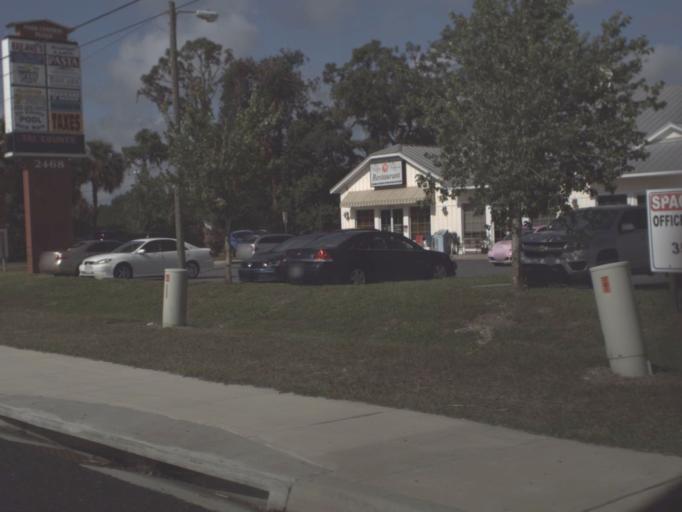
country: US
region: Florida
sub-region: Lake County
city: Fruitland Park
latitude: 28.8728
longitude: -81.9067
